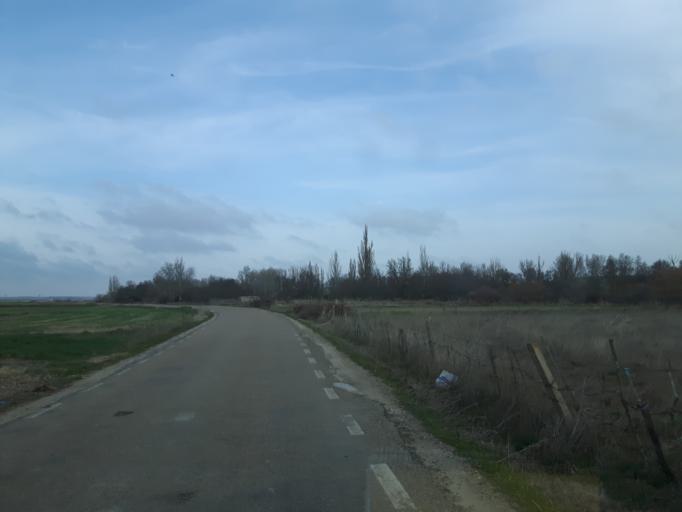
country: ES
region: Castille and Leon
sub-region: Provincia de Salamanca
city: Tordillos
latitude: 40.8575
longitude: -5.3562
